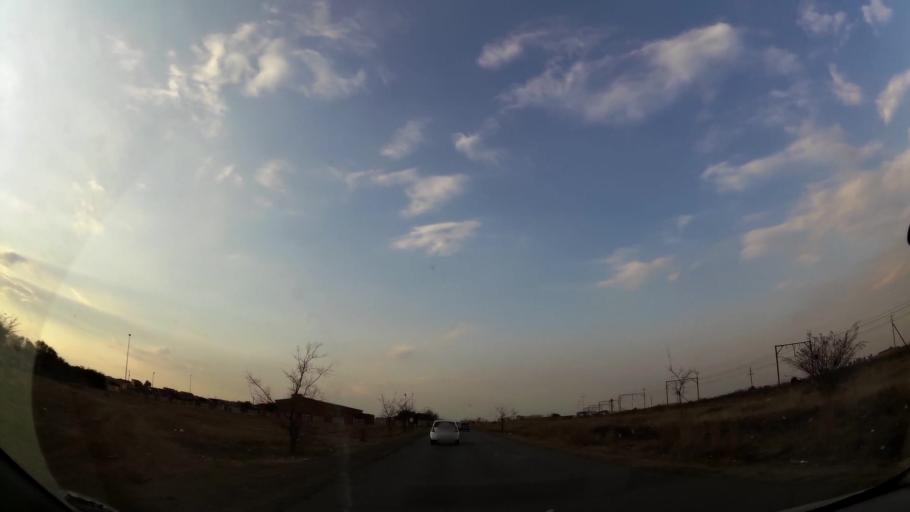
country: ZA
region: Gauteng
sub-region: City of Johannesburg Metropolitan Municipality
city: Orange Farm
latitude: -26.5688
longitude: 27.8608
